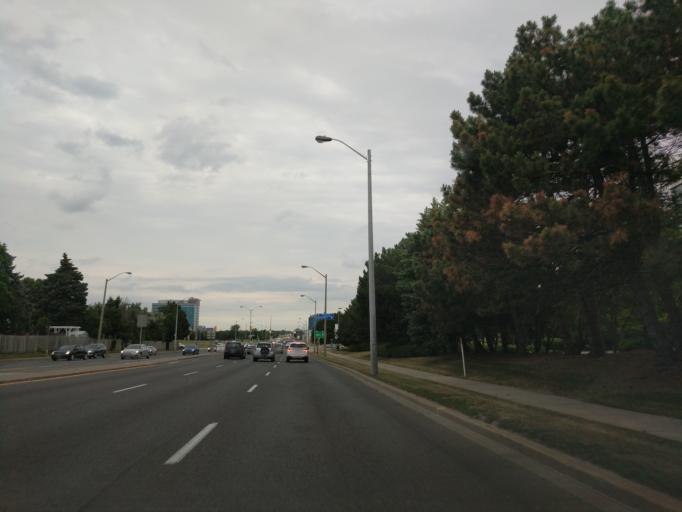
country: CA
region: Ontario
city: Willowdale
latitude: 43.8175
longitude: -79.3346
